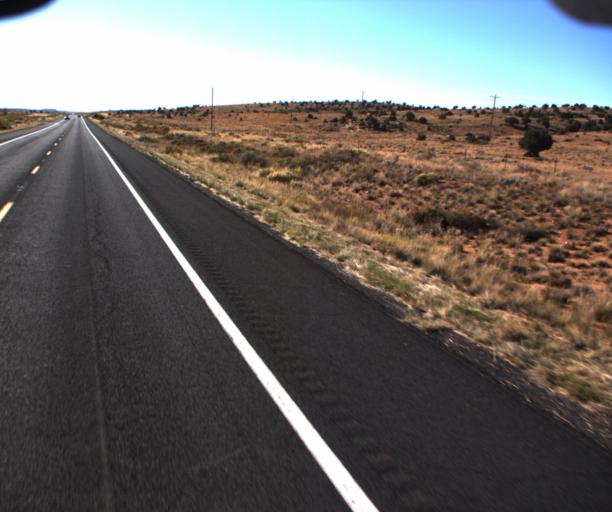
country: US
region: Arizona
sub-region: Coconino County
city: Tuba City
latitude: 36.3770
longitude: -111.5173
